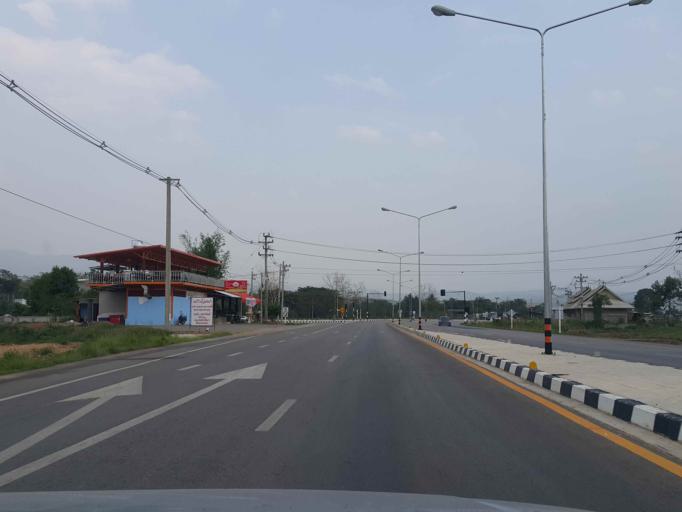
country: TH
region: Chiang Mai
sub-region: Amphoe Chiang Dao
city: Chiang Dao
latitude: 19.3498
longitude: 98.9597
